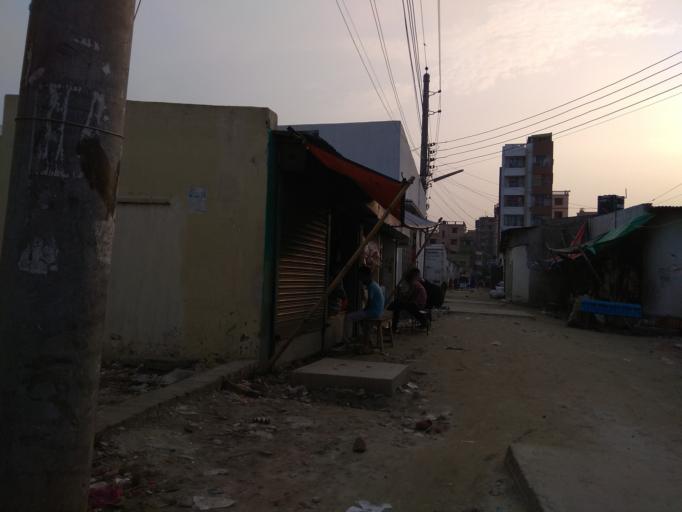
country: BD
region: Dhaka
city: Tungi
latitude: 23.8150
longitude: 90.3816
